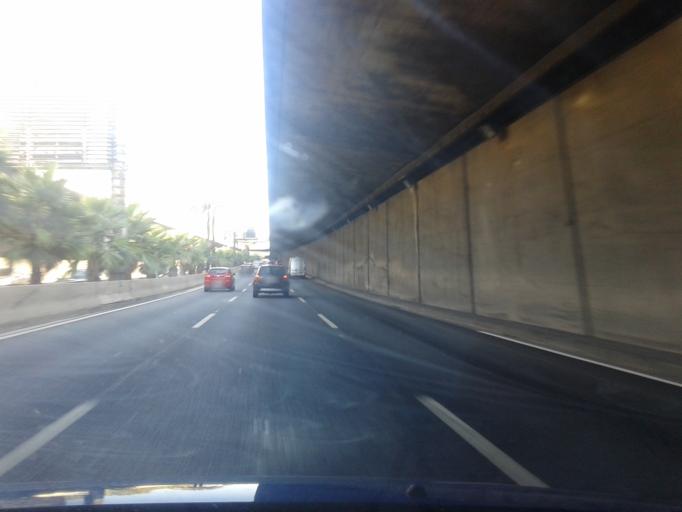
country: ES
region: Catalonia
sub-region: Provincia de Barcelona
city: Sarria-Sant Gervasi
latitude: 41.4178
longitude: 2.1390
